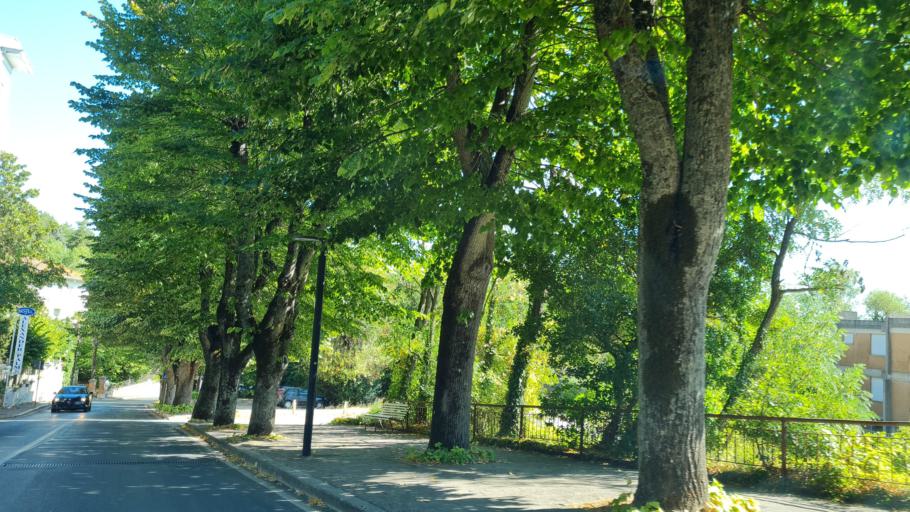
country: IT
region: Tuscany
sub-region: Provincia di Siena
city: Chianciano Terme
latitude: 43.0428
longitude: 11.8119
